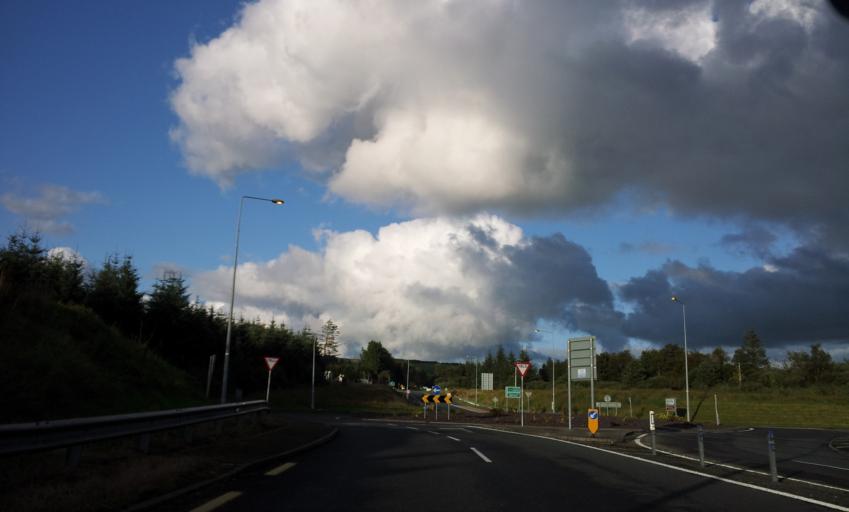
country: IE
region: Munster
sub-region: Ciarrai
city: Castleisland
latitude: 52.2602
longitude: -9.4640
